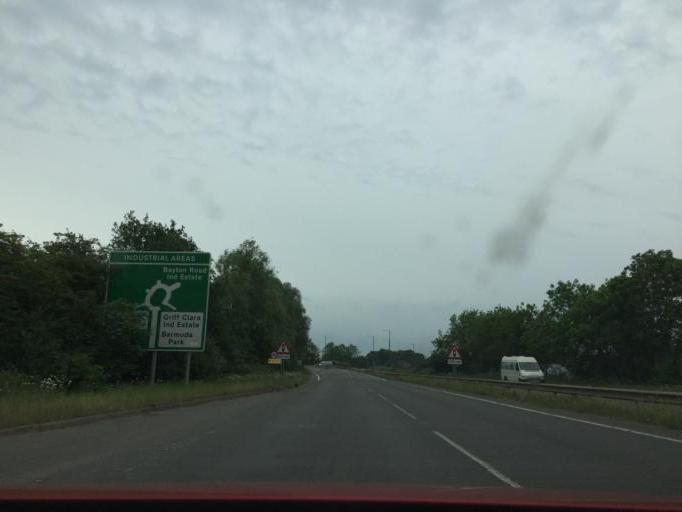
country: GB
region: England
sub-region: Warwickshire
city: Bedworth
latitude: 52.5011
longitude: -1.4751
